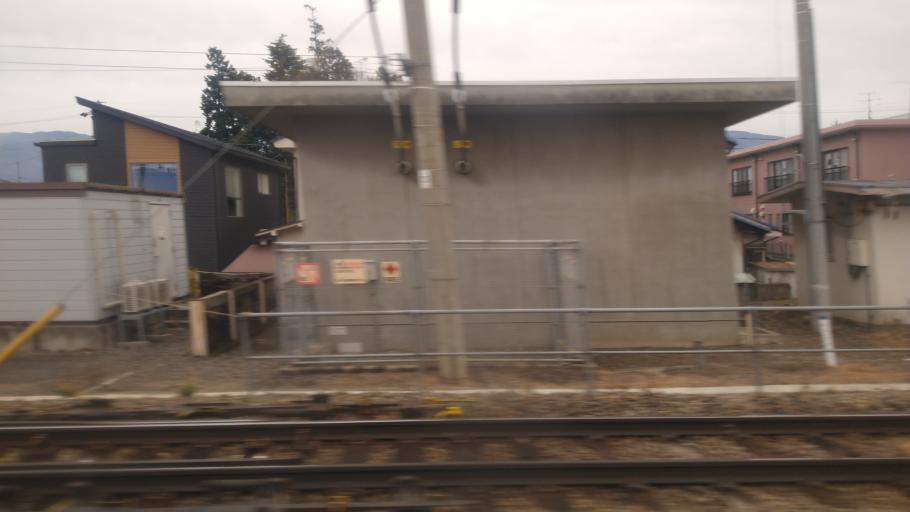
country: JP
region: Nagano
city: Matsumoto
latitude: 36.1757
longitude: 137.9566
